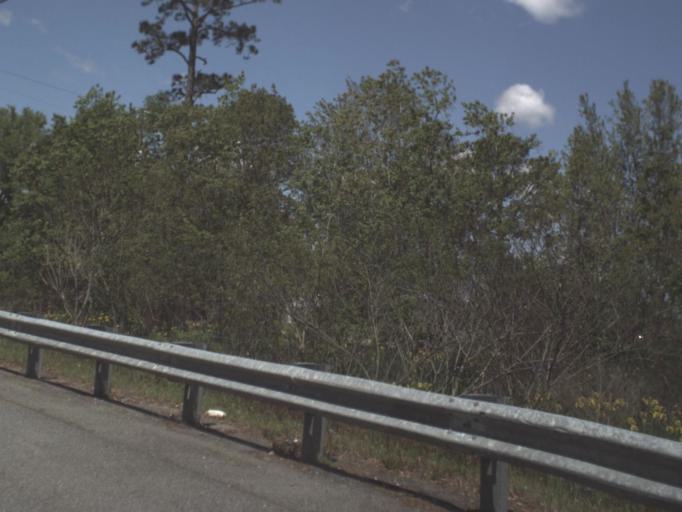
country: US
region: Florida
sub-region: Escambia County
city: Myrtle Grove
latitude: 30.4239
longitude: -87.3442
